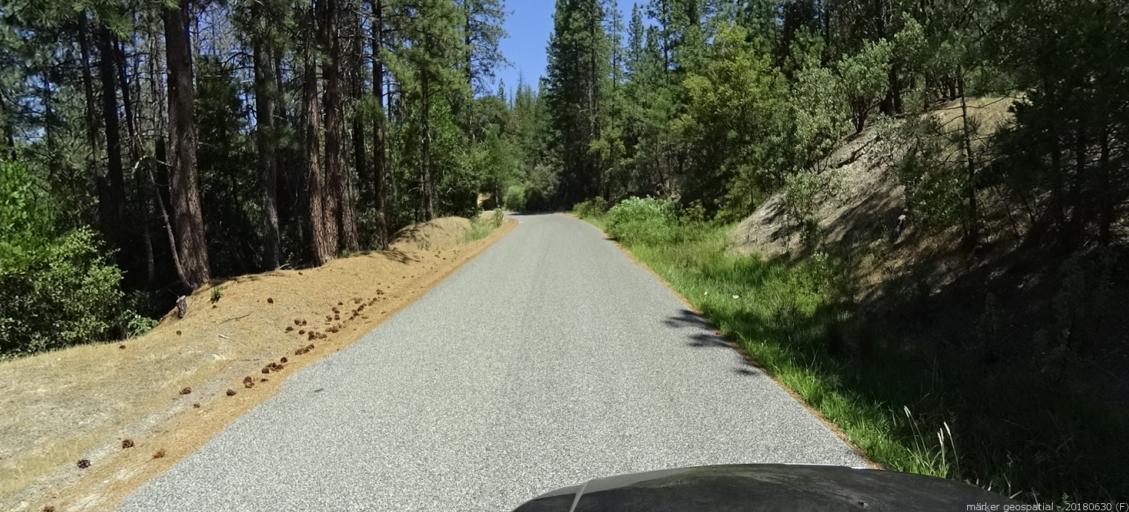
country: US
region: California
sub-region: Madera County
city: Oakhurst
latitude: 37.3788
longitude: -119.3614
